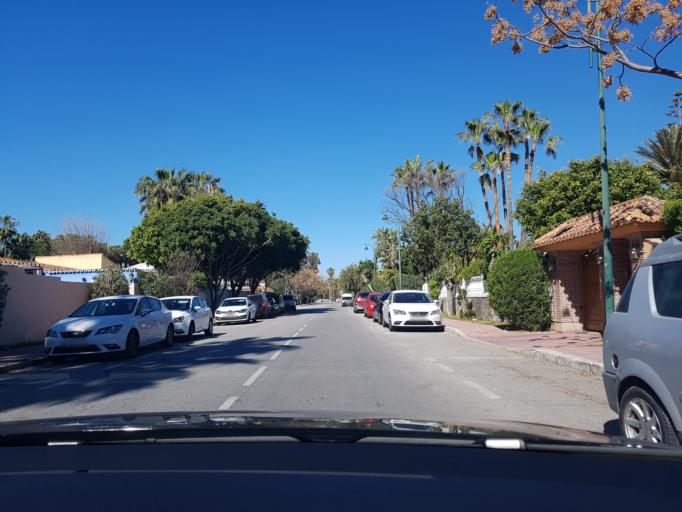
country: ES
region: Andalusia
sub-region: Provincia de Malaga
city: Torremolinos
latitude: 36.6667
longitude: -4.4581
